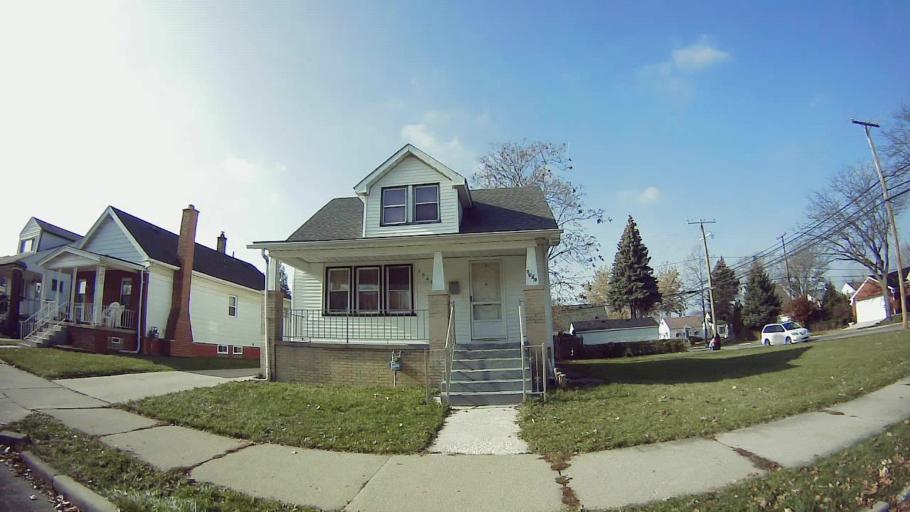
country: US
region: Michigan
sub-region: Wayne County
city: Dearborn
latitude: 42.3326
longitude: -83.1838
